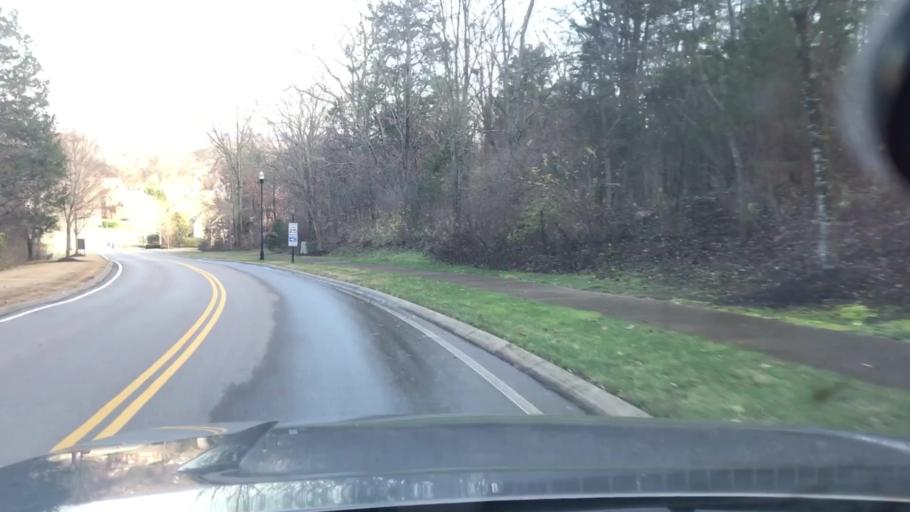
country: US
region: Tennessee
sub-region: Williamson County
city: Brentwood Estates
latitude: 35.9737
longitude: -86.7456
